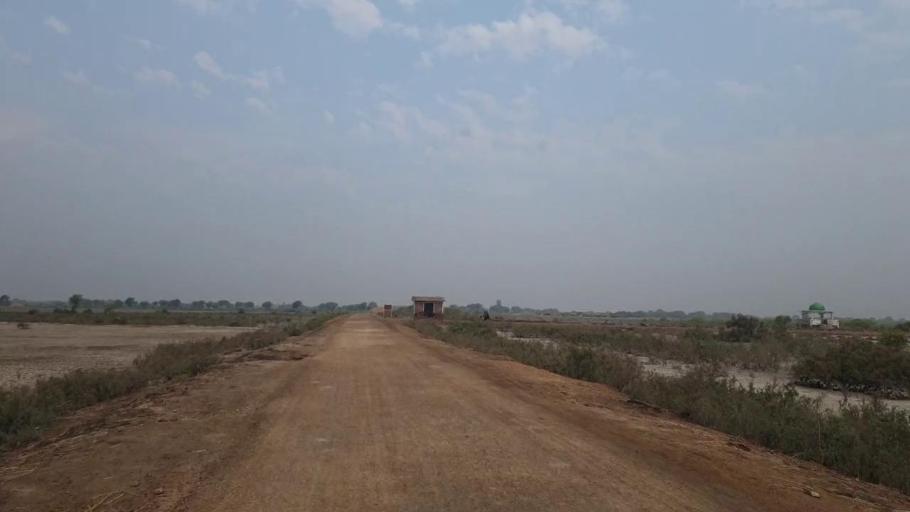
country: PK
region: Sindh
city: Tando Bago
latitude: 24.7999
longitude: 68.8750
